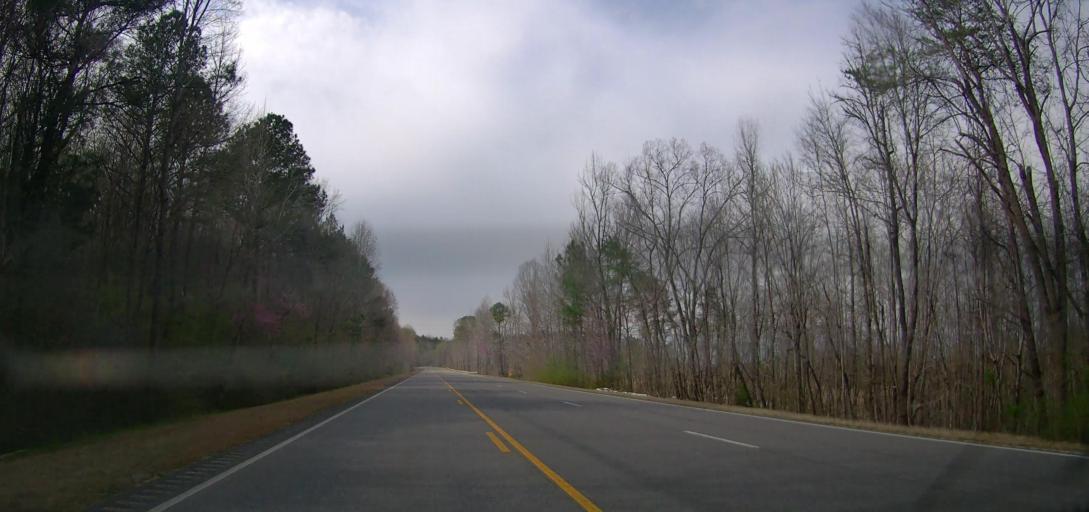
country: US
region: Alabama
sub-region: Walker County
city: Carbon Hill
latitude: 33.9130
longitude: -87.5623
